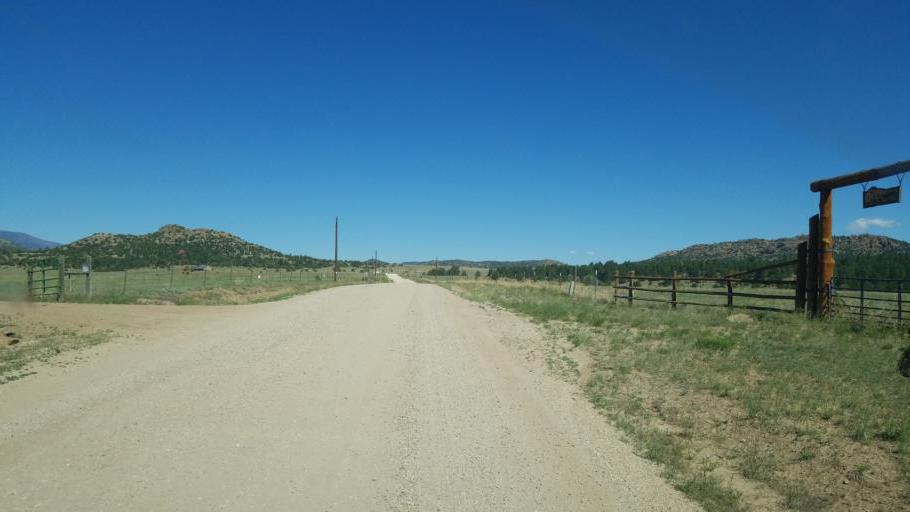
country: US
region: Colorado
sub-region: Custer County
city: Westcliffe
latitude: 38.2152
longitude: -105.4471
